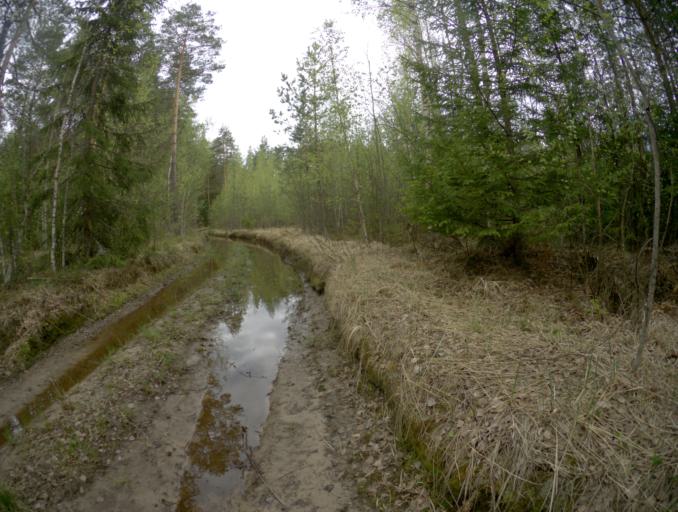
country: RU
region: Vladimir
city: Golovino
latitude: 55.9196
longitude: 40.4102
